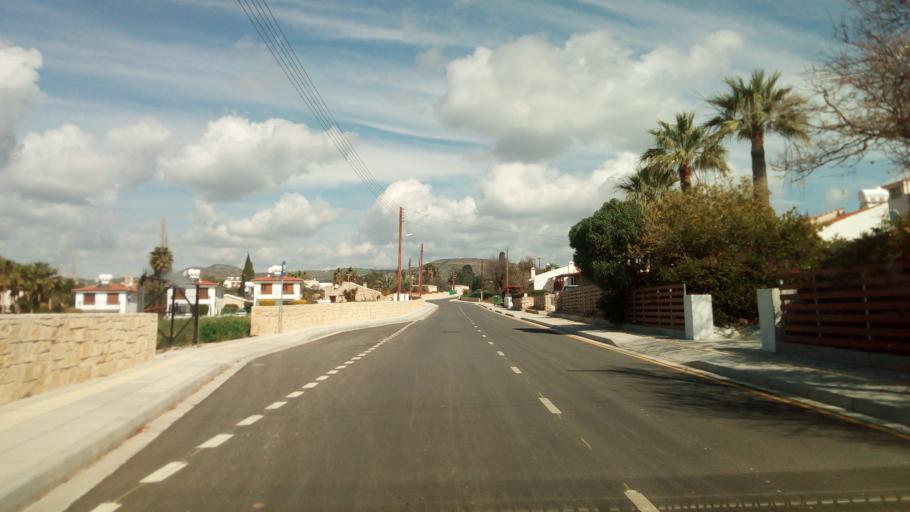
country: CY
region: Pafos
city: Mesogi
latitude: 34.7367
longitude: 32.5340
